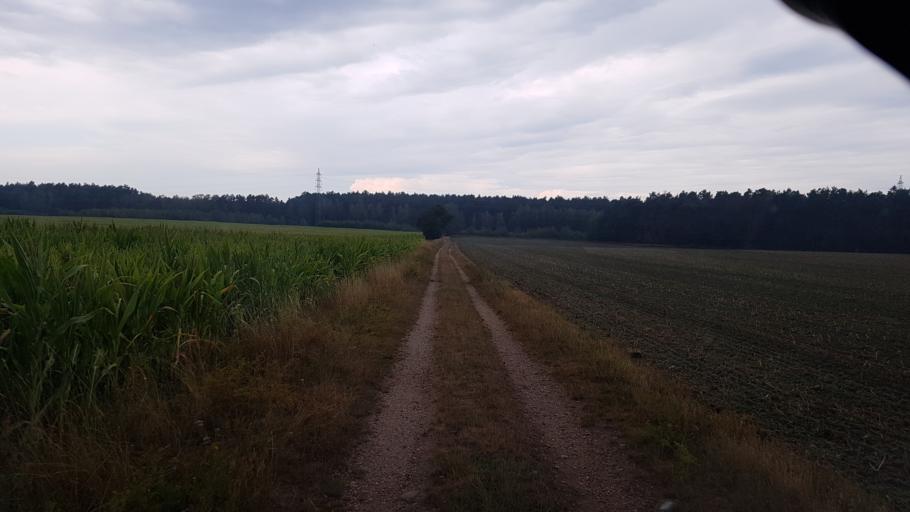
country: DE
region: Brandenburg
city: Finsterwalde
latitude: 51.6355
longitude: 13.7621
